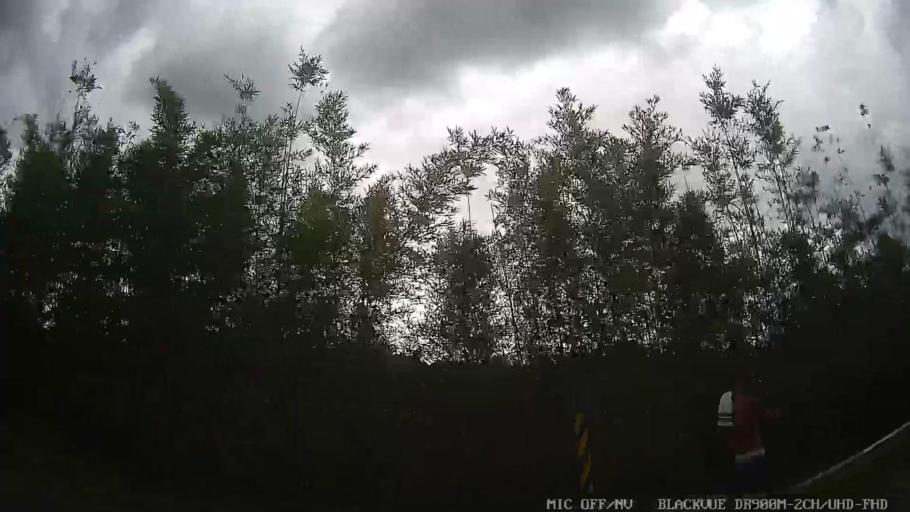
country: BR
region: Sao Paulo
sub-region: Suzano
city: Suzano
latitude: -23.6044
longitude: -46.3011
